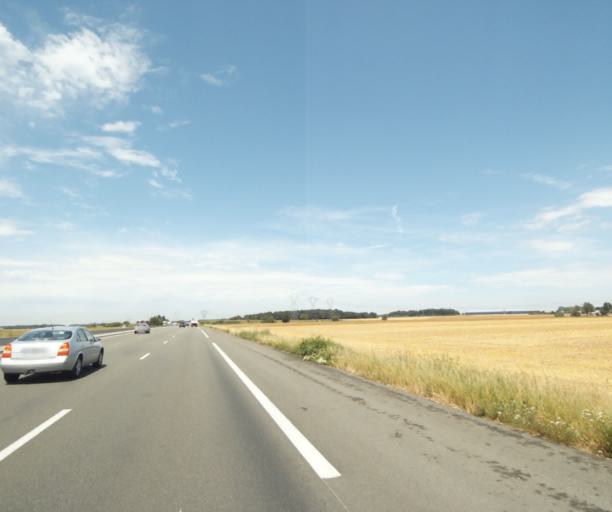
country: FR
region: Ile-de-France
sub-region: Departement de l'Essonne
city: Le Coudray-Montceaux
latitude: 48.5227
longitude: 2.5038
